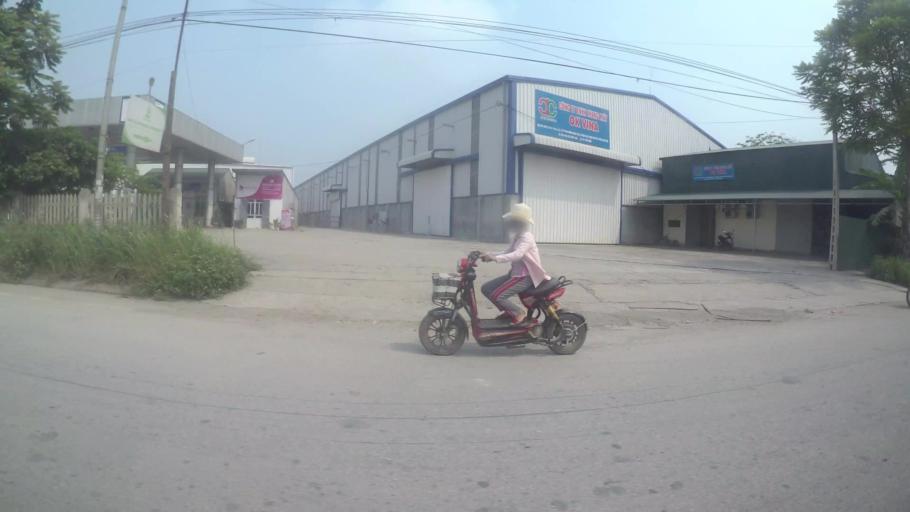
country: VN
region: Ha Noi
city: Quoc Oai
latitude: 21.0006
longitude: 105.5992
